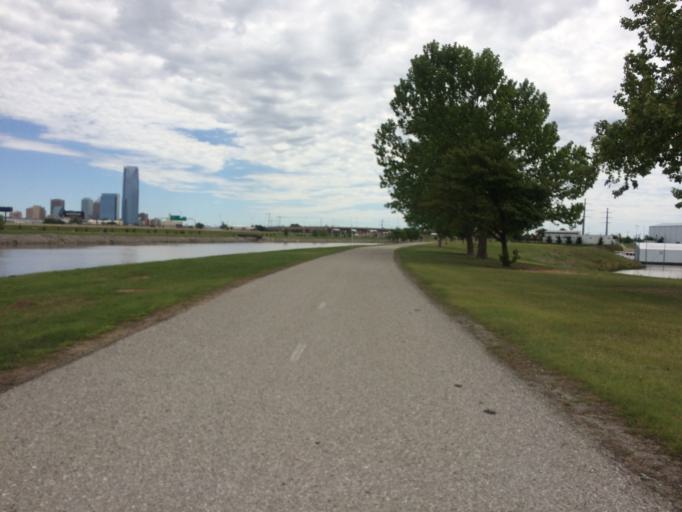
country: US
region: Oklahoma
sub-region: Oklahoma County
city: Oklahoma City
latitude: 35.4594
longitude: -97.5441
